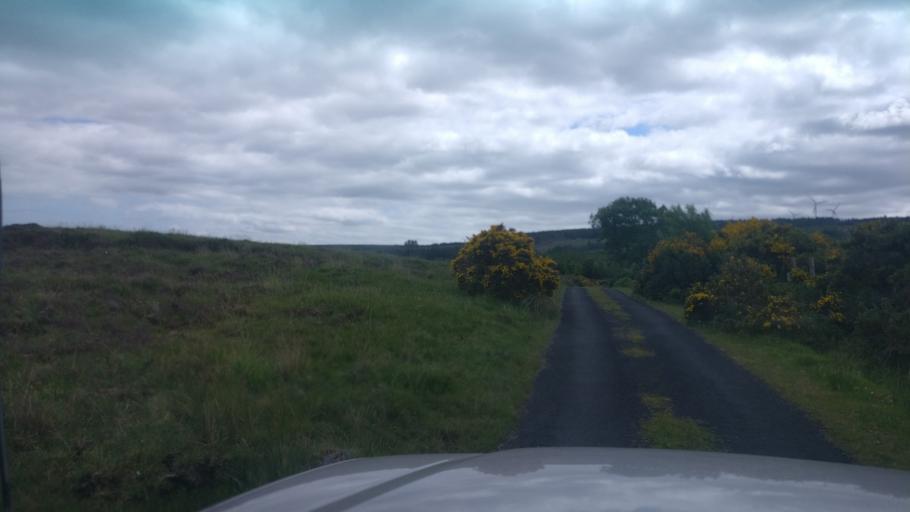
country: IE
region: Connaught
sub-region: County Galway
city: Loughrea
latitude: 53.1132
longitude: -8.6306
